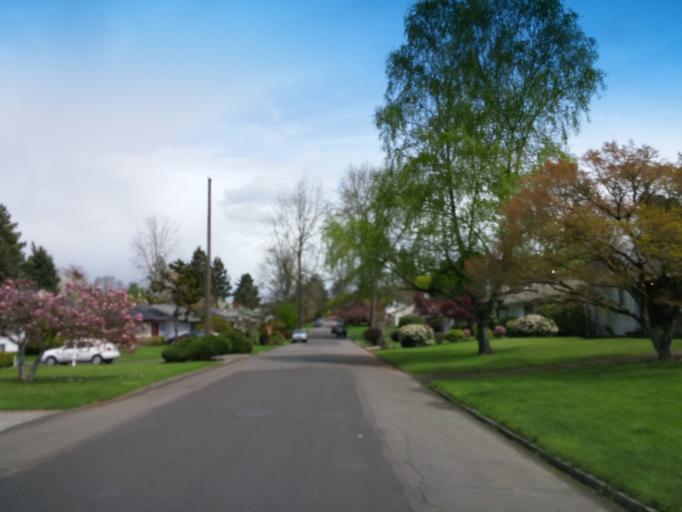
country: US
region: Oregon
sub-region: Washington County
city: Cedar Hills
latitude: 45.5040
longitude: -122.8032
